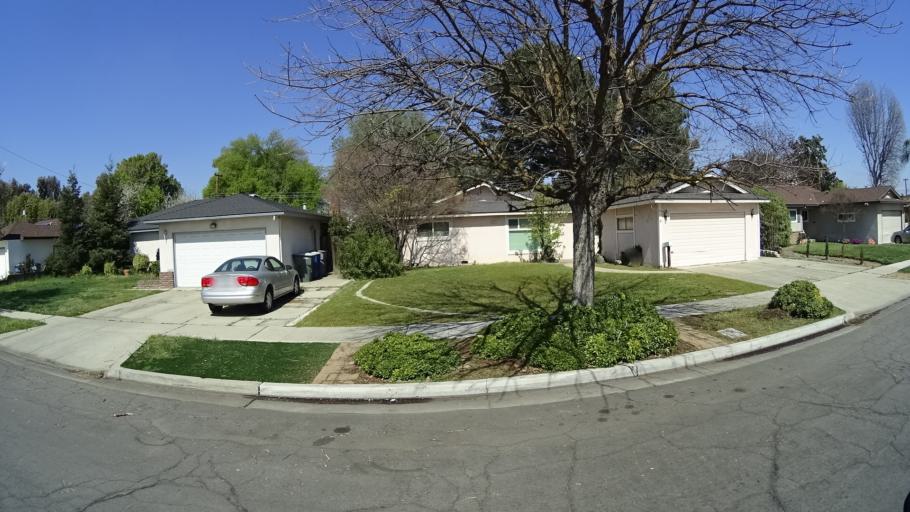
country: US
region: California
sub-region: Fresno County
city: Tarpey Village
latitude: 36.8045
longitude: -119.7341
